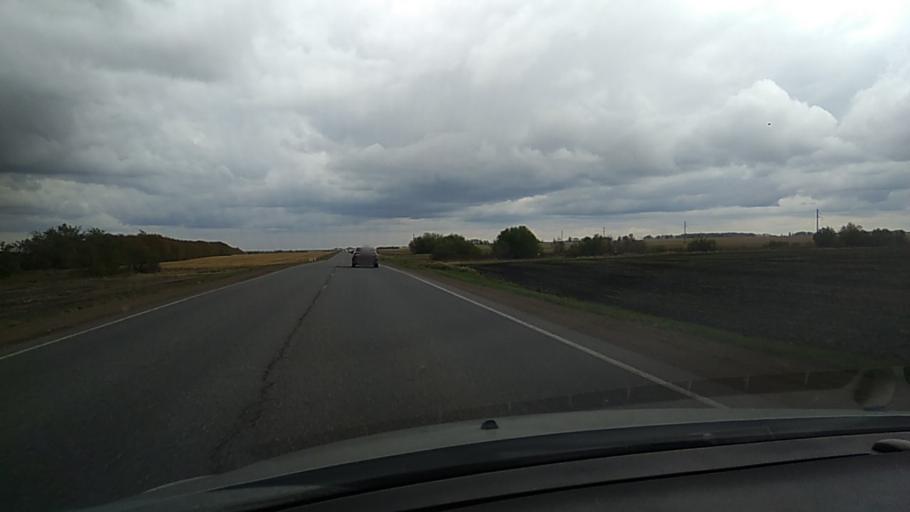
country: RU
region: Kurgan
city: Dalmatovo
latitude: 56.2896
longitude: 62.8058
